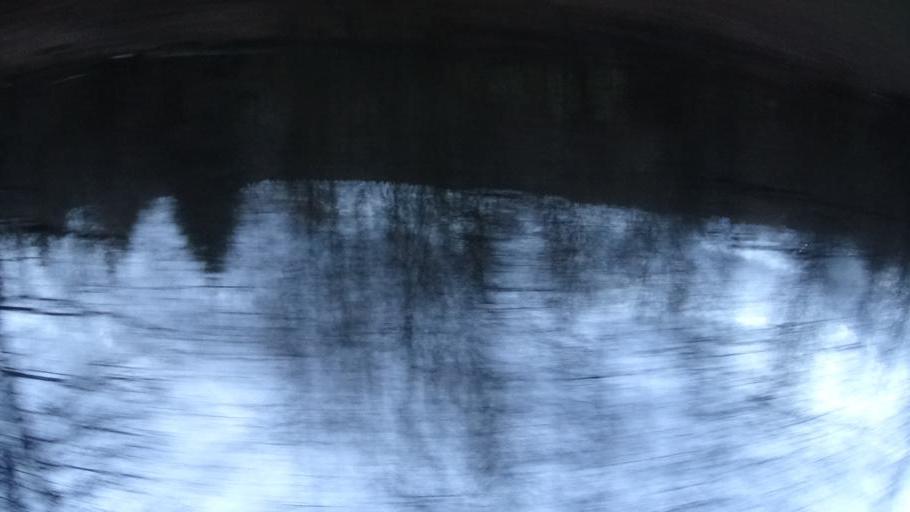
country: DE
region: Hesse
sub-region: Regierungsbezirk Kassel
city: Eichenzell
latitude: 50.4518
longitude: 9.7262
